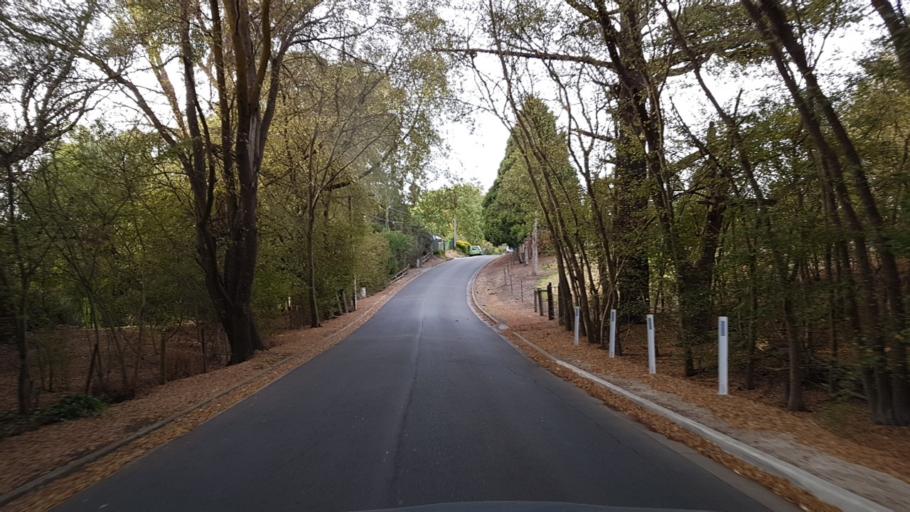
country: AU
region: South Australia
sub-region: Mount Barker
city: Nairne
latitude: -35.0339
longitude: 138.9101
